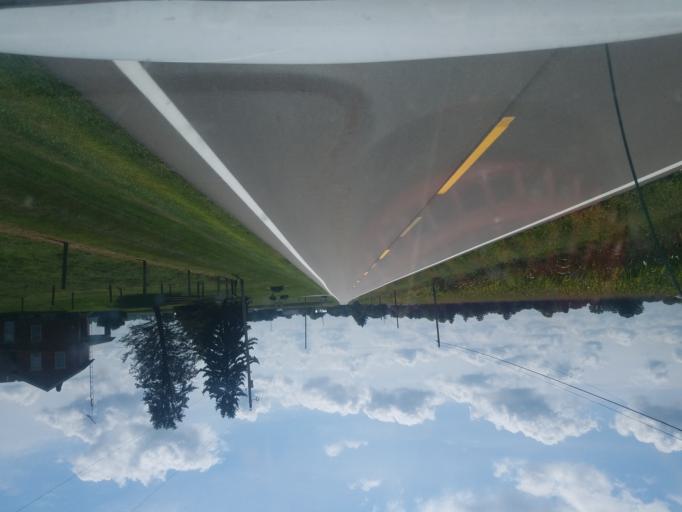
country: US
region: Ohio
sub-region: Marion County
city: Prospect
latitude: 40.3896
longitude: -83.1539
